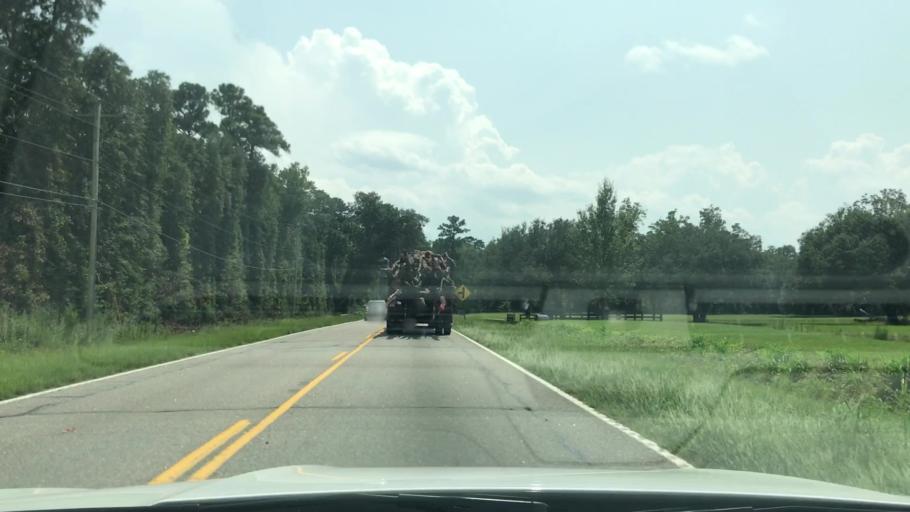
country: US
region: South Carolina
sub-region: Georgetown County
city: Georgetown
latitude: 33.4642
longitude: -79.2804
